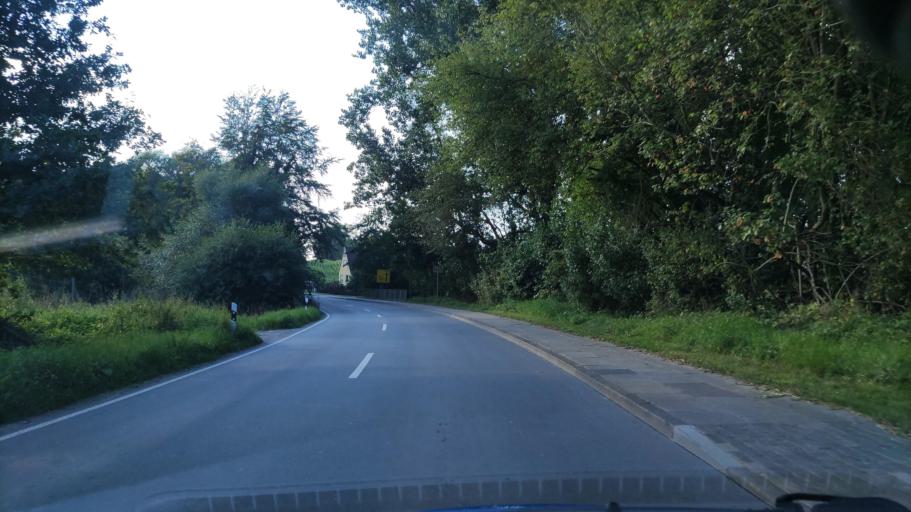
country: DE
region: Schleswig-Holstein
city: Glasau
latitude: 54.0587
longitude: 10.5237
